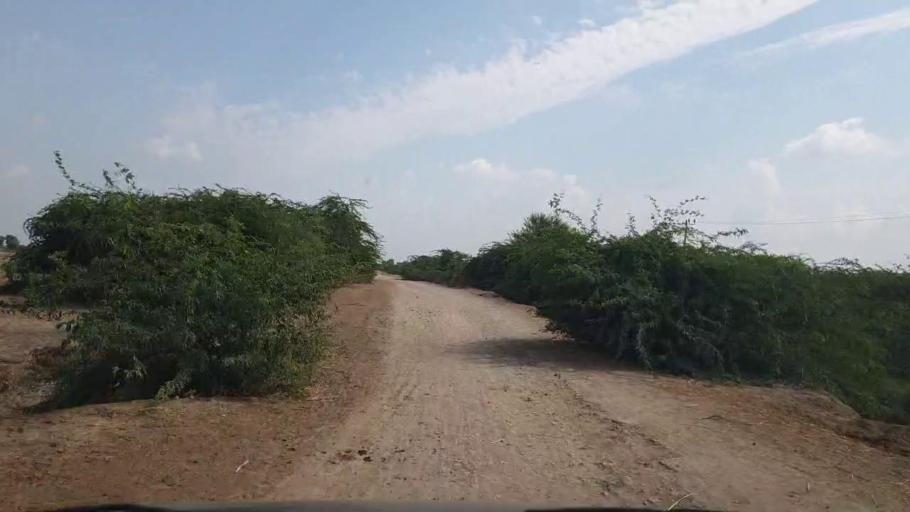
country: PK
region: Sindh
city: Badin
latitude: 24.4775
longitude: 68.6219
